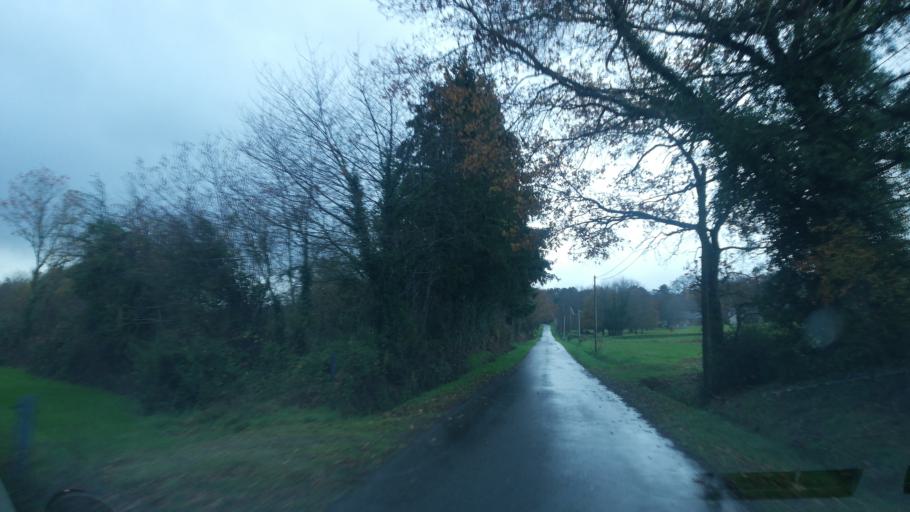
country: FR
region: Brittany
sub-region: Departement d'Ille-et-Vilaine
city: Guignen
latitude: 47.8762
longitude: -1.8494
